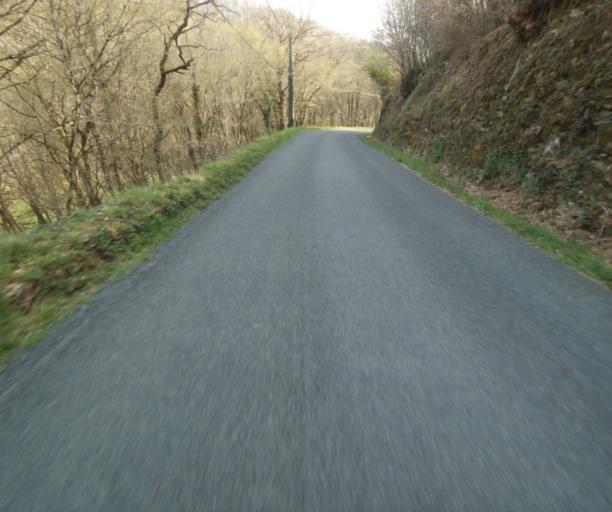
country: FR
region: Limousin
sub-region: Departement de la Correze
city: Naves
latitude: 45.3349
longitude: 1.7913
